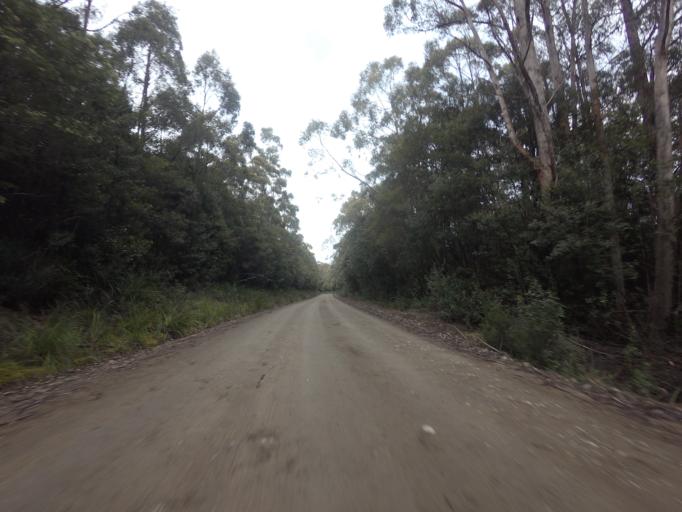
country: AU
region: Tasmania
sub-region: Huon Valley
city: Geeveston
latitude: -43.5014
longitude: 146.8779
